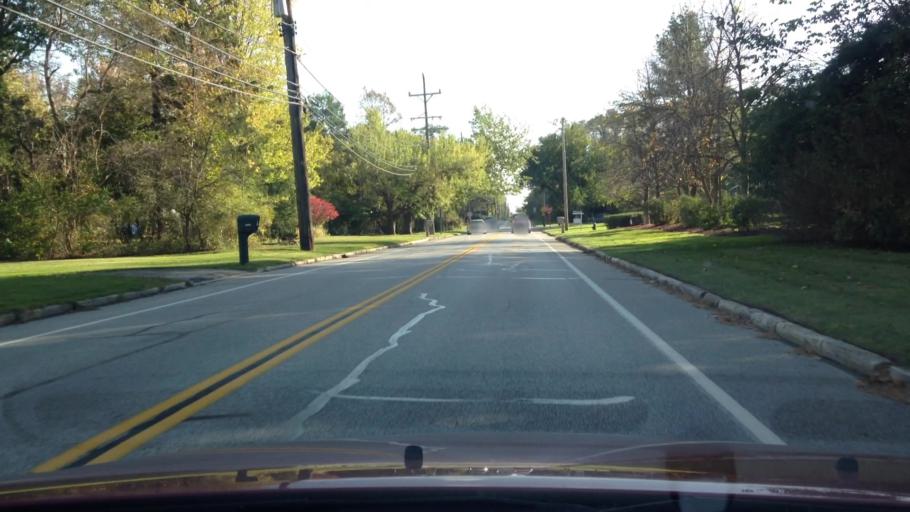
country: US
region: Ohio
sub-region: Cuyahoga County
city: Pepper Pike
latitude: 41.4798
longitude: -81.4633
